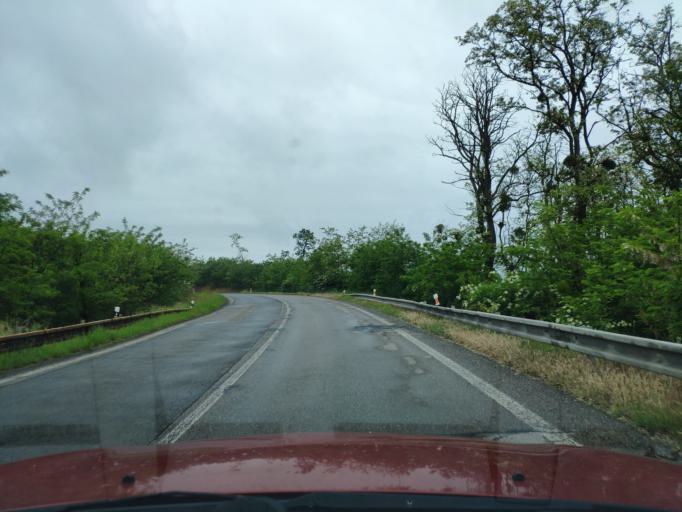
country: HU
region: Borsod-Abauj-Zemplen
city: Ricse
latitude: 48.4412
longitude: 21.9438
